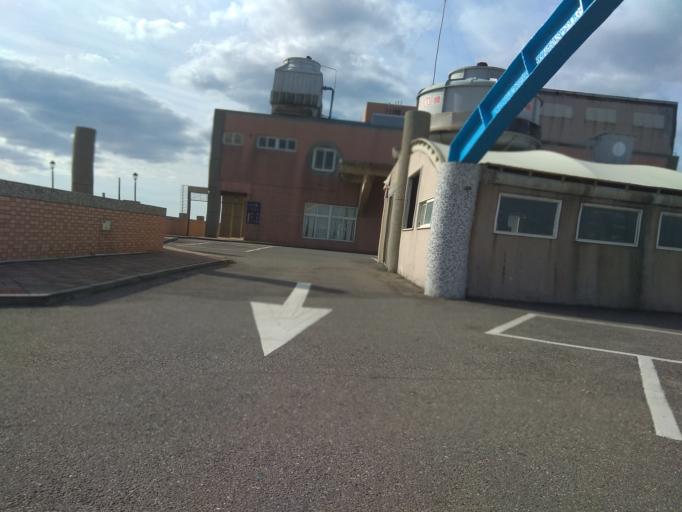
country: TW
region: Taiwan
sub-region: Hsinchu
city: Zhubei
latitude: 24.9877
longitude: 121.0155
